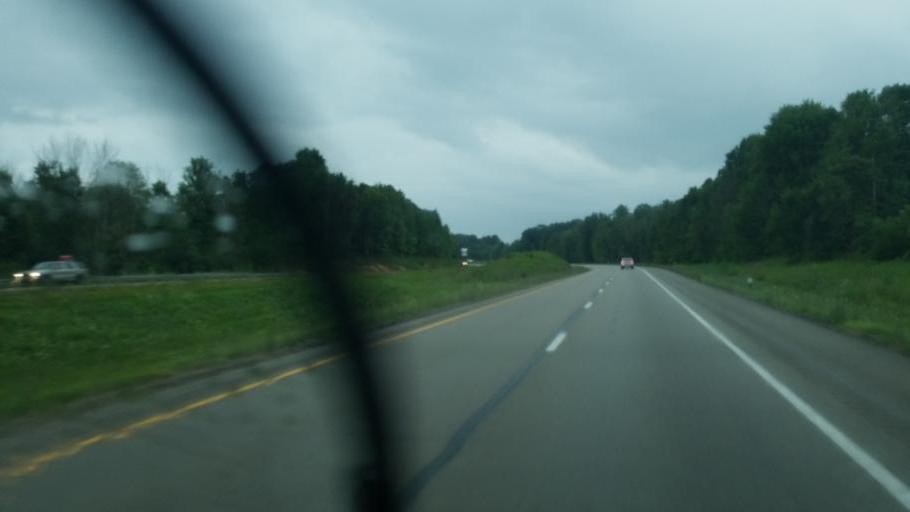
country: US
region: Pennsylvania
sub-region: Mercer County
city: Grove City
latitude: 41.1846
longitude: -80.1676
